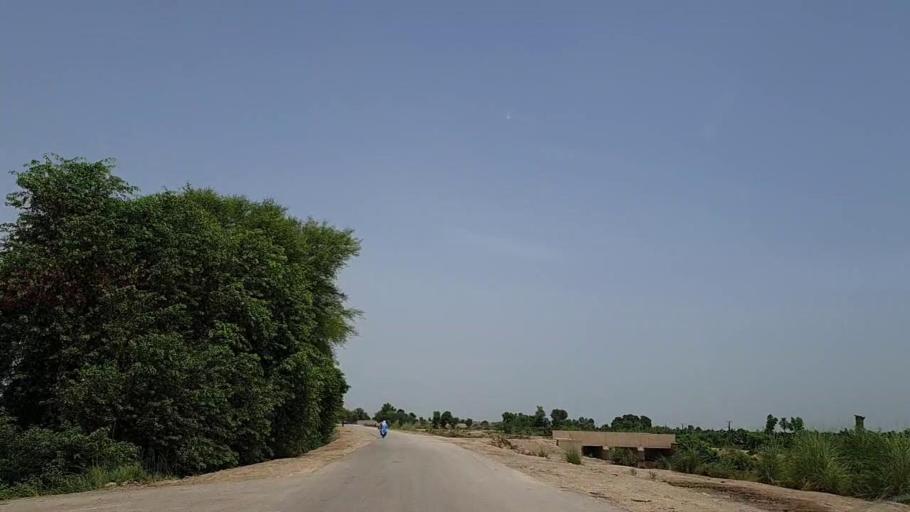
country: PK
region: Sindh
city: Tharu Shah
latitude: 26.8892
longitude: 68.0118
